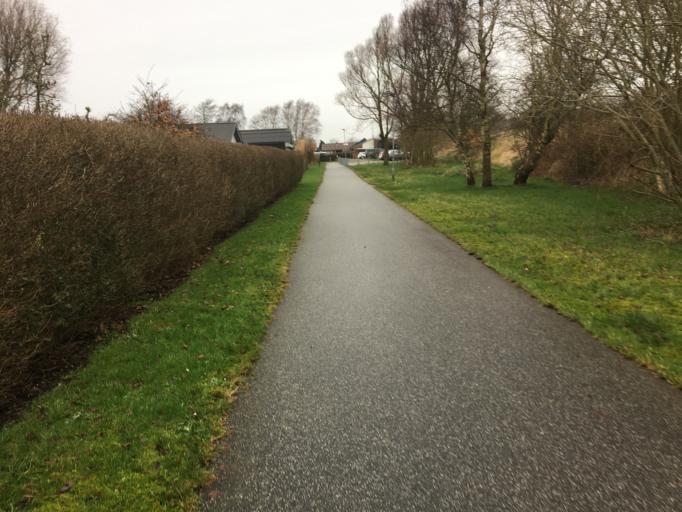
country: DK
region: Central Jutland
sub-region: Ringkobing-Skjern Kommune
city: Ringkobing
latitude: 56.0937
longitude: 8.2555
